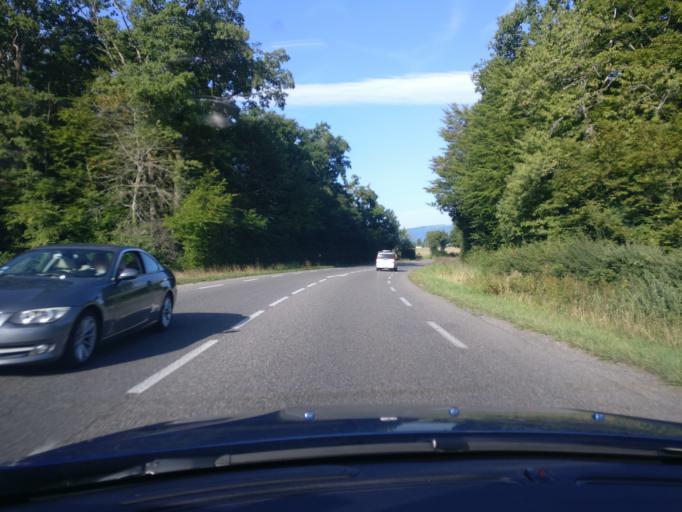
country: FR
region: Rhone-Alpes
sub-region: Departement de l'Ain
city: Ferney-Voltaire
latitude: 46.2489
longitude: 6.1078
